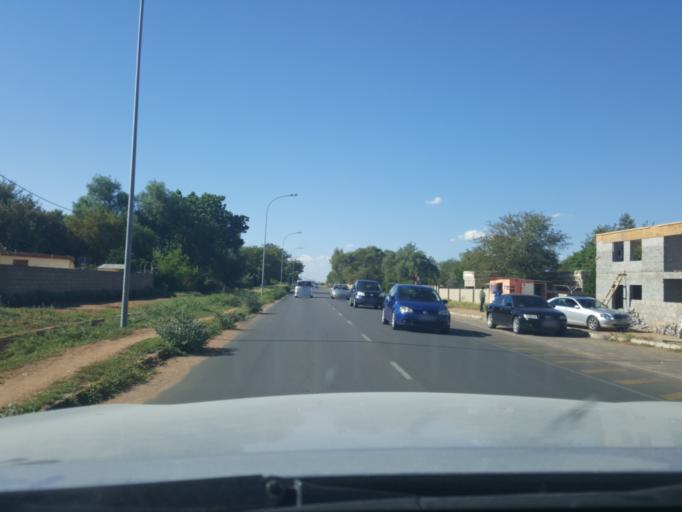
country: BW
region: South East
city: Gaborone
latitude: -24.6201
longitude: 25.9444
